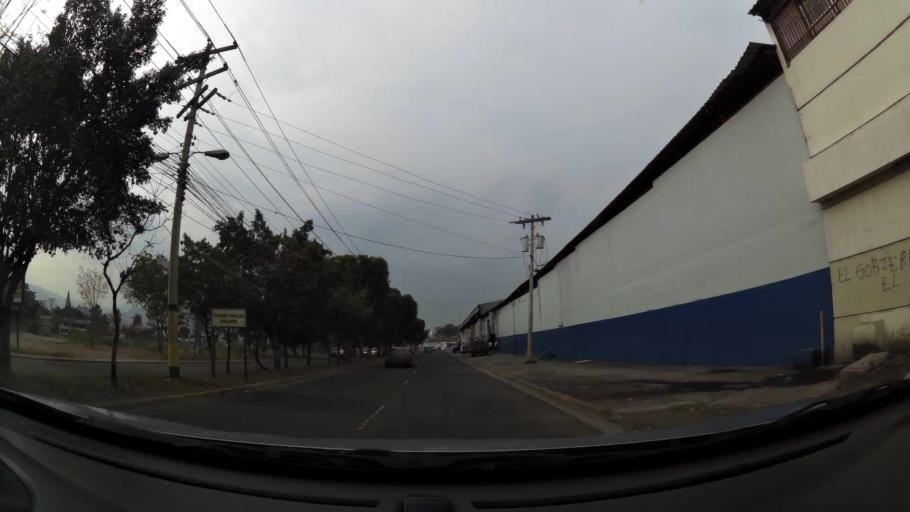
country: HN
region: Francisco Morazan
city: Tegucigalpa
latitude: 14.0797
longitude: -87.2030
